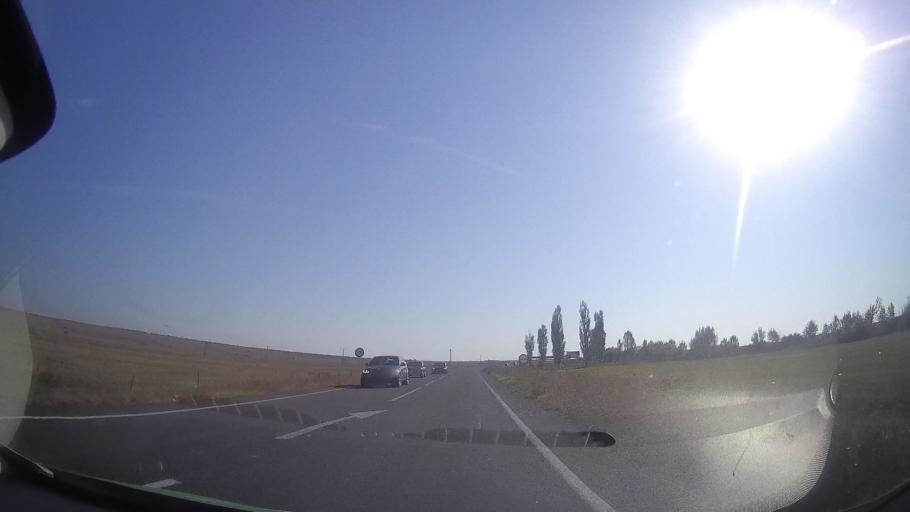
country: RO
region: Timis
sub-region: Comuna Topolovatu Mare
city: Topolovatu Mare
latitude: 45.7839
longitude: 21.5964
